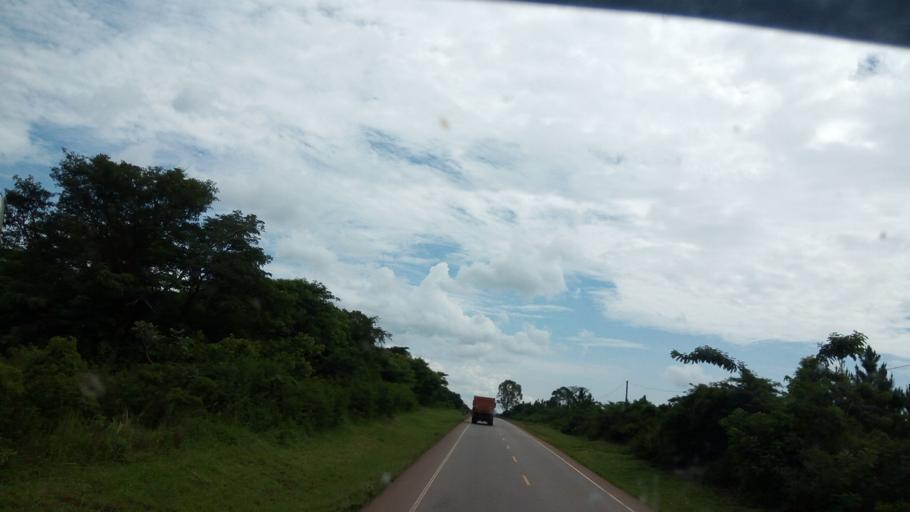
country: UG
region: Central Region
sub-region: Nakasongola District
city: Nakasongola
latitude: 1.1741
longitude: 32.4625
